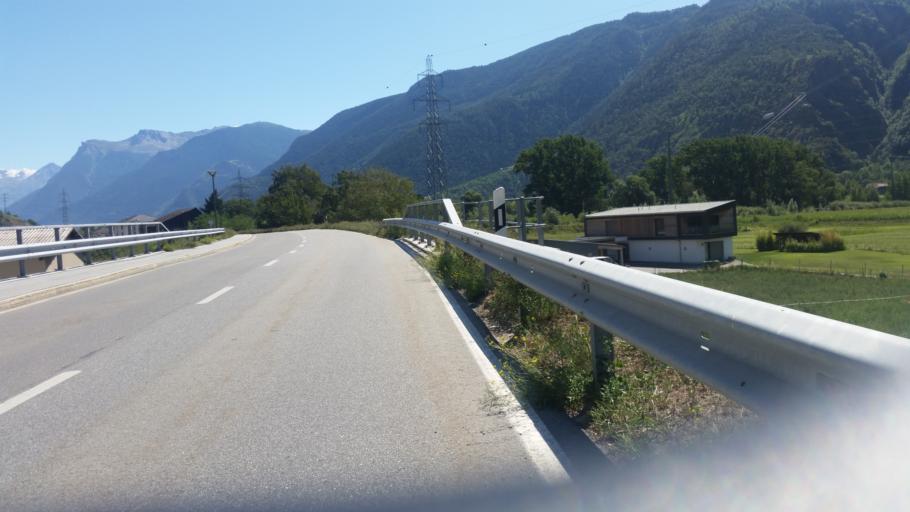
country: CH
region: Valais
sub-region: Raron District
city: Raron
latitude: 46.3093
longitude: 7.7939
